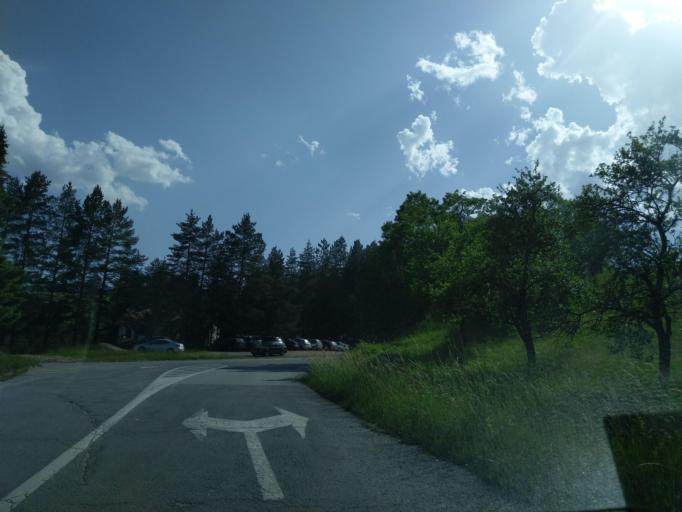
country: RS
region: Central Serbia
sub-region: Zlatiborski Okrug
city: Bajina Basta
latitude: 43.8435
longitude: 19.6032
